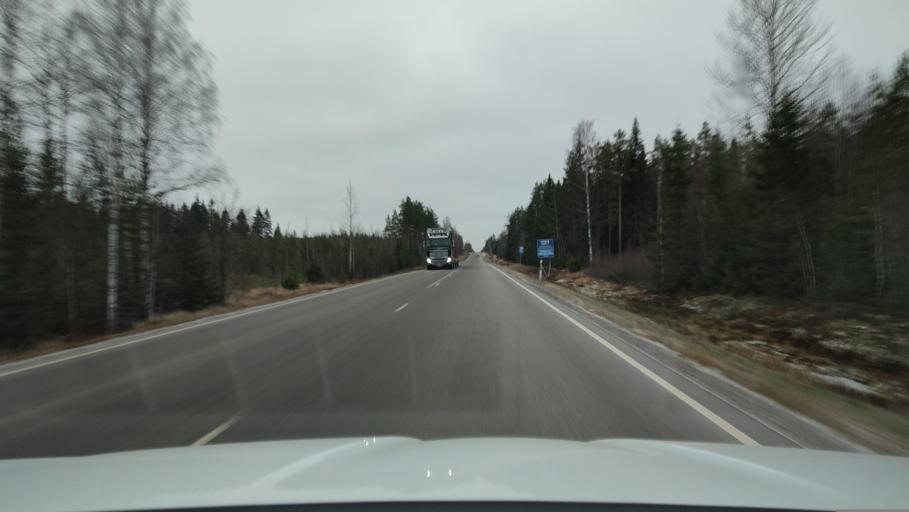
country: FI
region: Ostrobothnia
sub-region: Sydosterbotten
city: Naerpes
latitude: 62.4991
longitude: 21.4479
